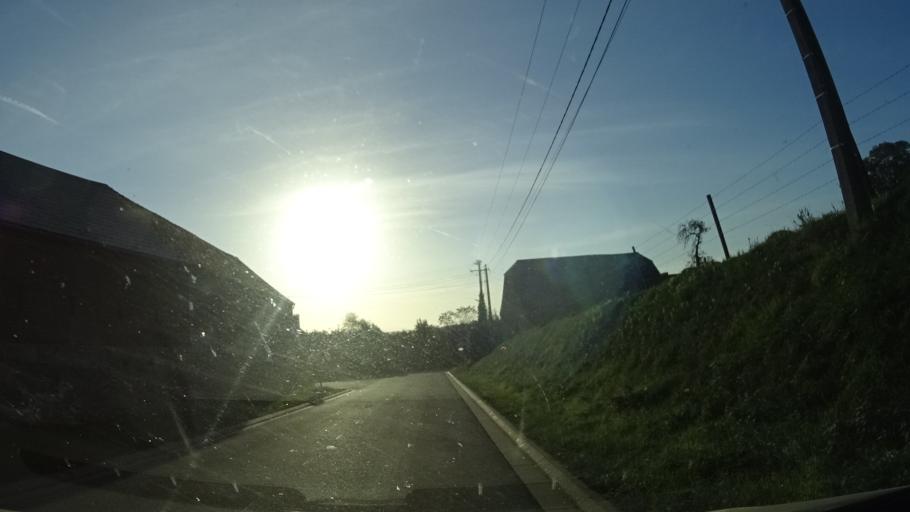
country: BE
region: Wallonia
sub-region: Province du Hainaut
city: Beaumont
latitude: 50.2641
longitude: 4.2283
